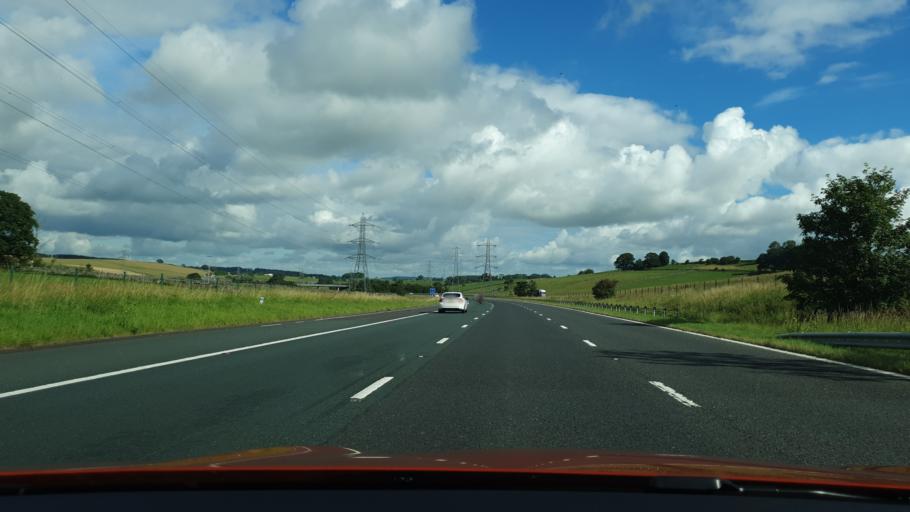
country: GB
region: England
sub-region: Cumbria
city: Penrith
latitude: 54.5543
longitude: -2.6731
